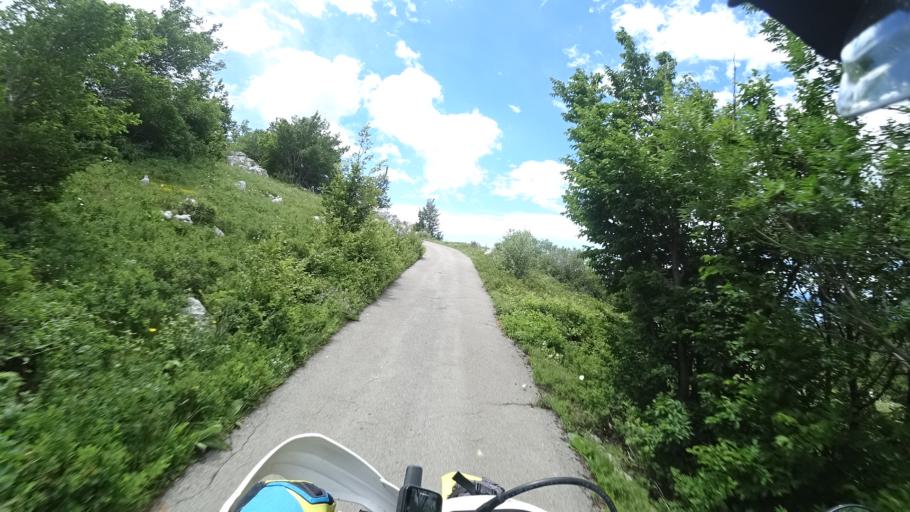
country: HR
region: Primorsko-Goranska
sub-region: Grad Crikvenica
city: Jadranovo
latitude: 45.2475
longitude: 14.6704
